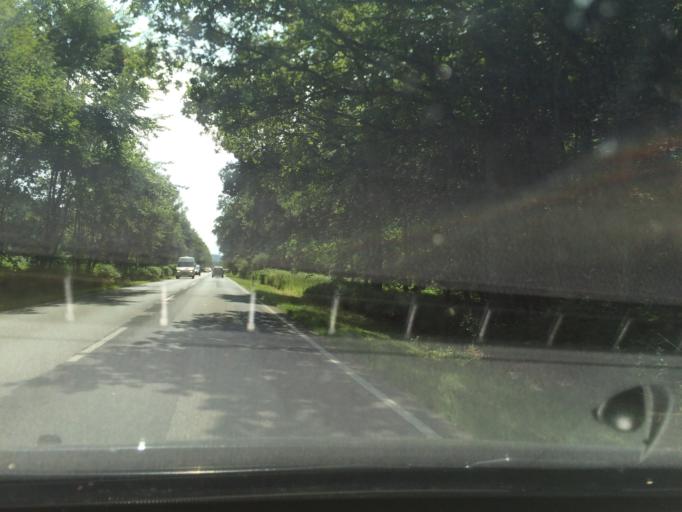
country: DE
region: Mecklenburg-Vorpommern
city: Ostseebad Binz
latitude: 54.4188
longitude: 13.5856
